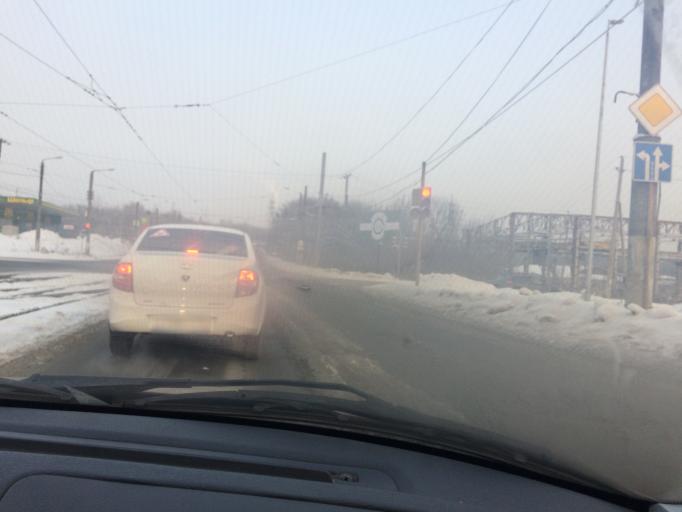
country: RU
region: Chelyabinsk
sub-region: Gorod Magnitogorsk
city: Magnitogorsk
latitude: 53.4502
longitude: 59.0568
